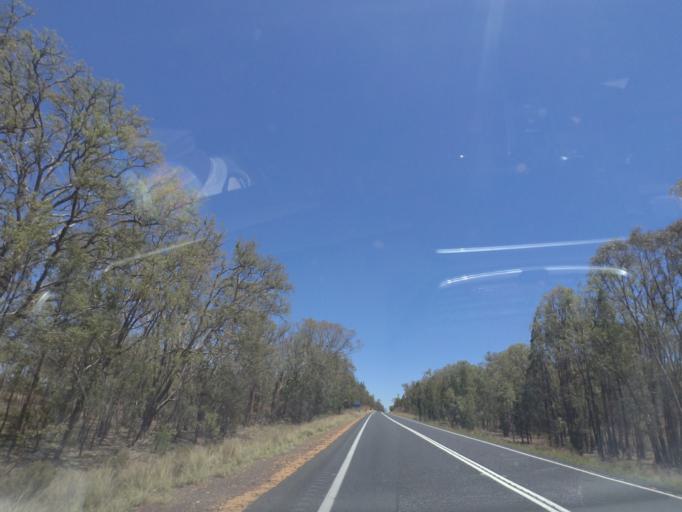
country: AU
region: New South Wales
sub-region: Warrumbungle Shire
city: Coonabarabran
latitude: -31.2275
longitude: 149.3214
